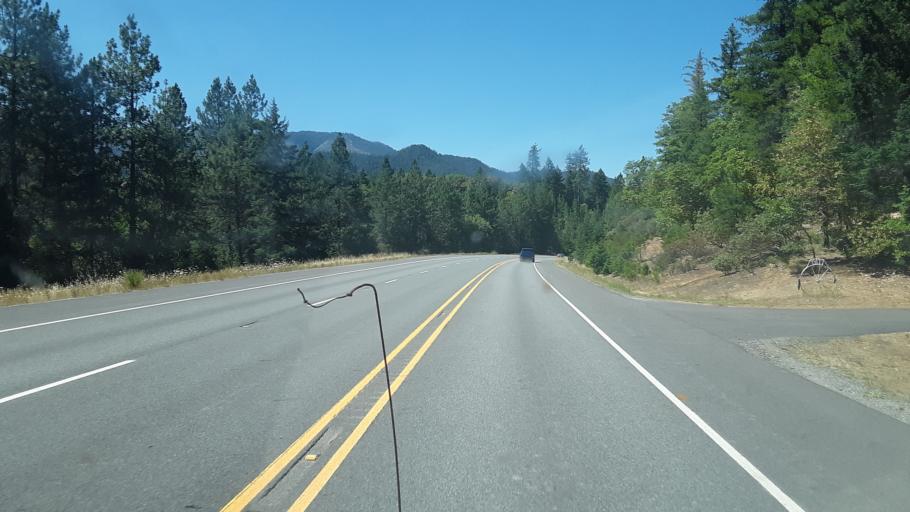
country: US
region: Oregon
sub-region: Josephine County
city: Cave Junction
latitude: 42.2664
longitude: -123.6193
